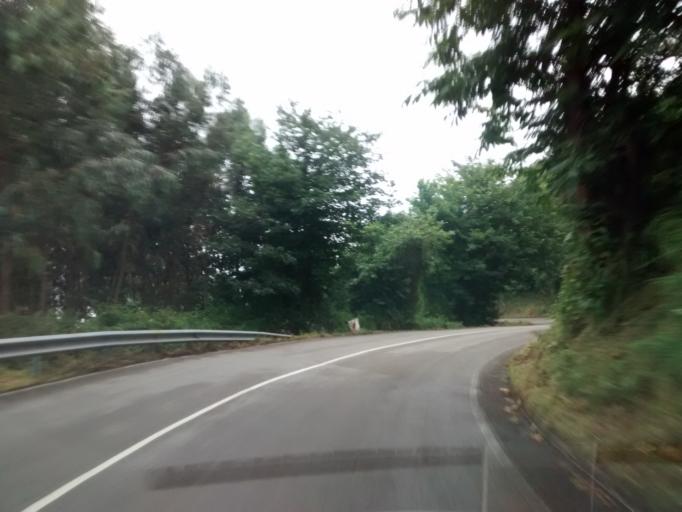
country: ES
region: Asturias
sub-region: Province of Asturias
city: Villaviciosa
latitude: 43.5317
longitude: -5.3952
